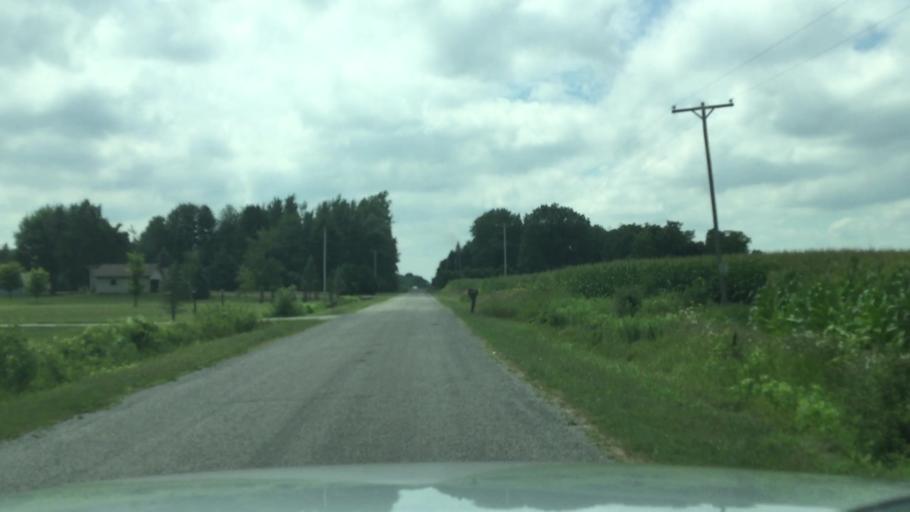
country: US
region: Michigan
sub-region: Saginaw County
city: Birch Run
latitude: 43.2977
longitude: -83.8347
